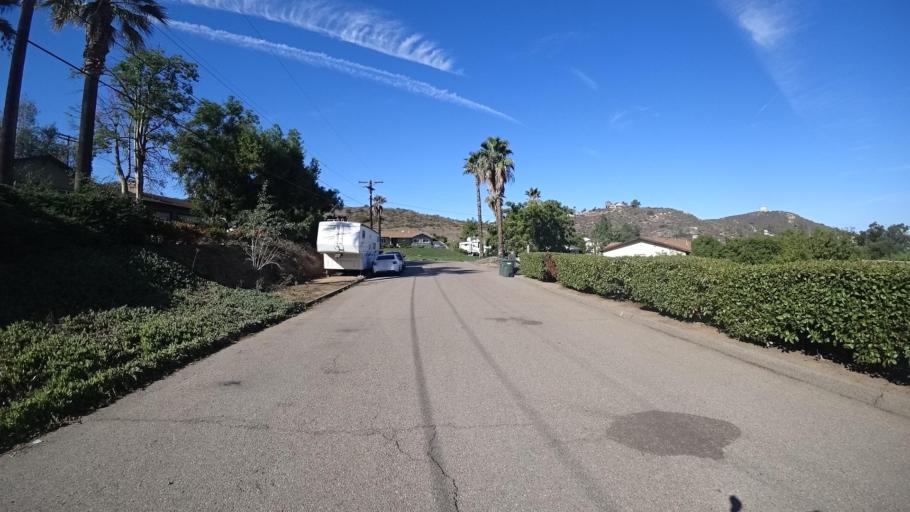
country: US
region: California
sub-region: San Diego County
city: Granite Hills
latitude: 32.8246
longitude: -116.9086
